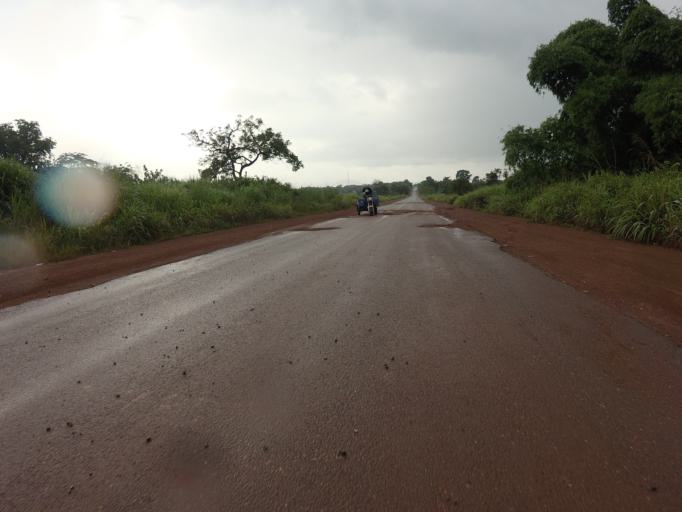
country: GH
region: Volta
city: Hohoe
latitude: 7.0331
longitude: 0.4272
